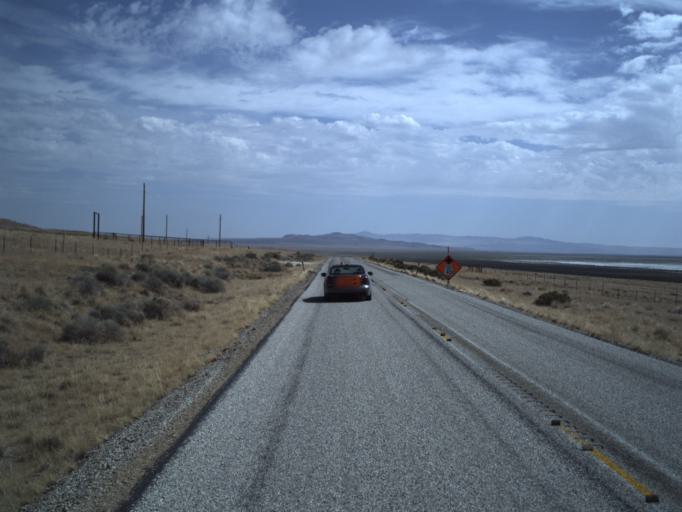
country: US
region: Utah
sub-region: Tooele County
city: Wendover
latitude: 41.4404
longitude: -113.7093
